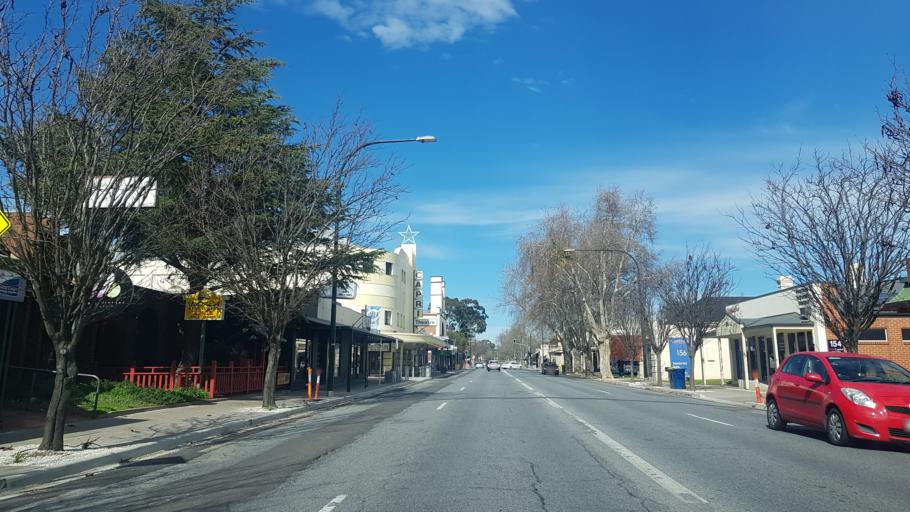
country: AU
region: South Australia
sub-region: Unley
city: Millswood
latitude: -34.9521
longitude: 138.5897
